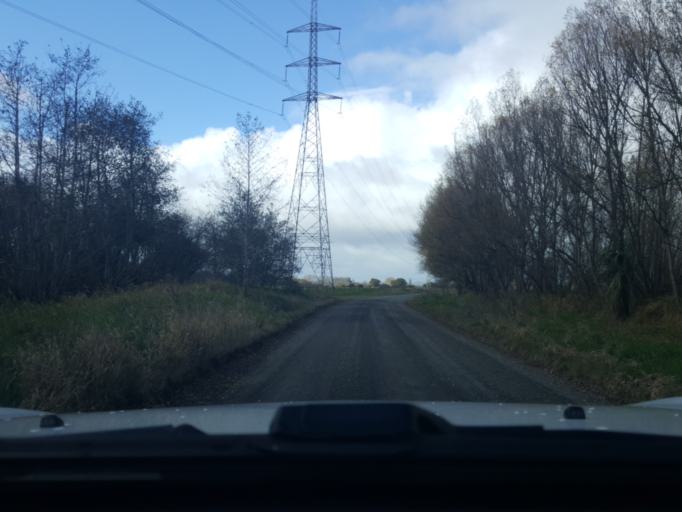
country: NZ
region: Waikato
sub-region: Waikato District
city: Te Kauwhata
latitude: -37.4124
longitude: 175.0613
